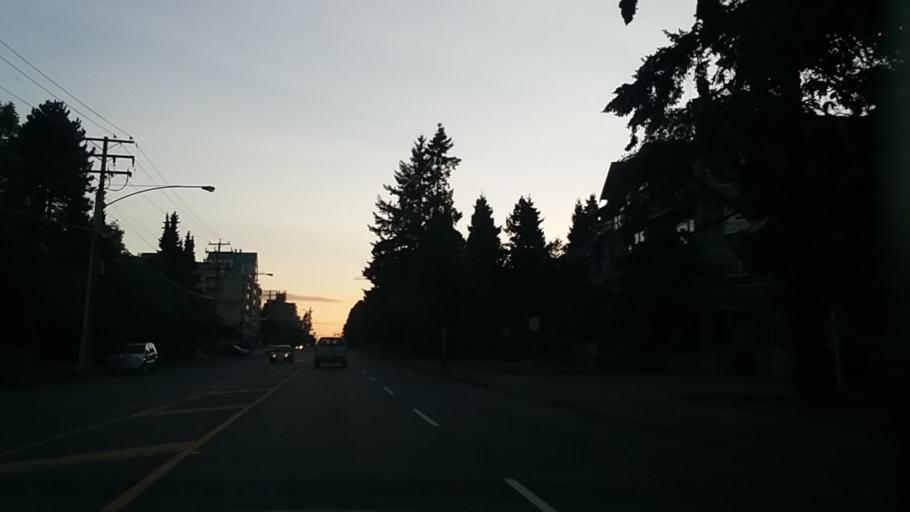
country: CA
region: British Columbia
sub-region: Greater Vancouver Regional District
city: White Rock
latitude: 49.0312
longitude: -122.7913
